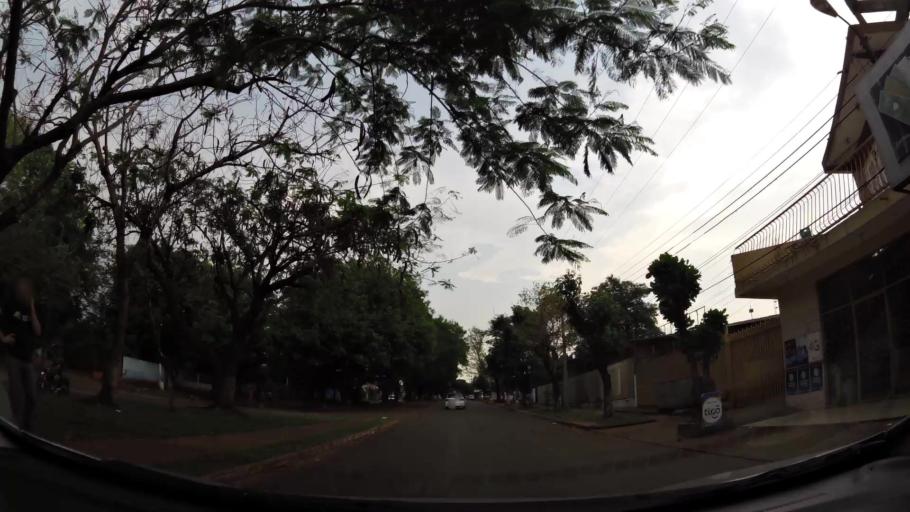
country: BR
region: Parana
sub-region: Foz Do Iguacu
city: Foz do Iguacu
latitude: -25.5421
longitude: -54.6016
